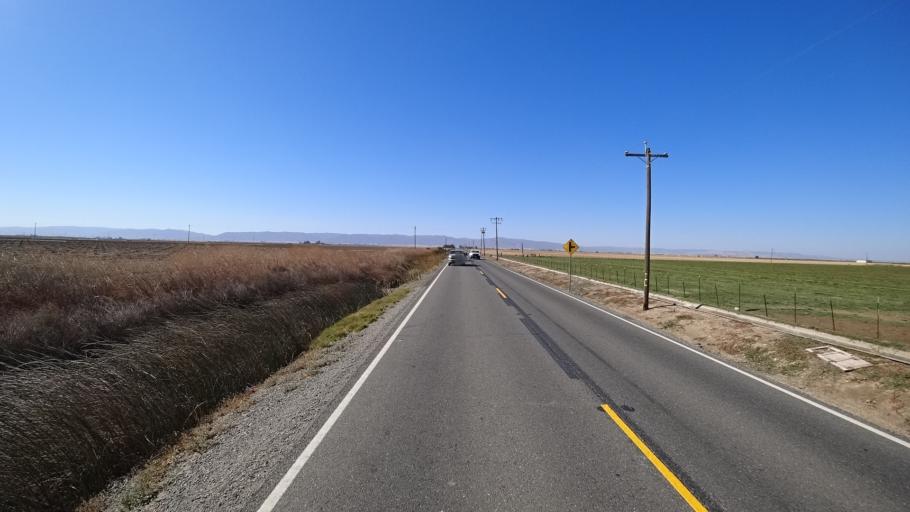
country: US
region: California
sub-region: Yolo County
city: Cottonwood
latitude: 38.6198
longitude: -121.8937
